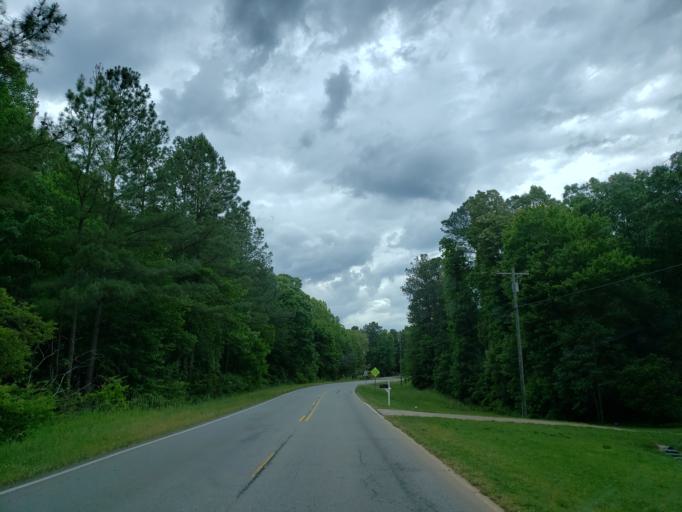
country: US
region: Georgia
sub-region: Polk County
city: Rockmart
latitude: 33.9438
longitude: -85.0455
